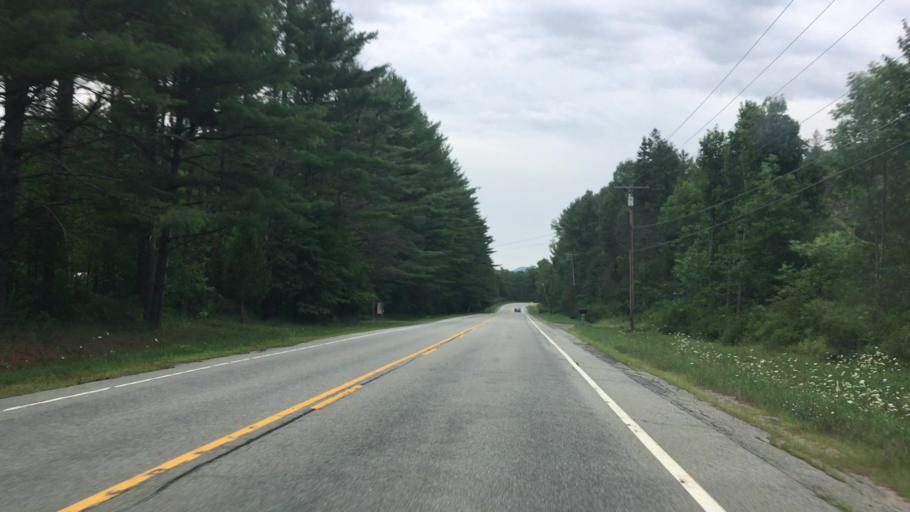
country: US
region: New York
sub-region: Essex County
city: Lake Placid
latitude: 44.2698
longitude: -73.7908
